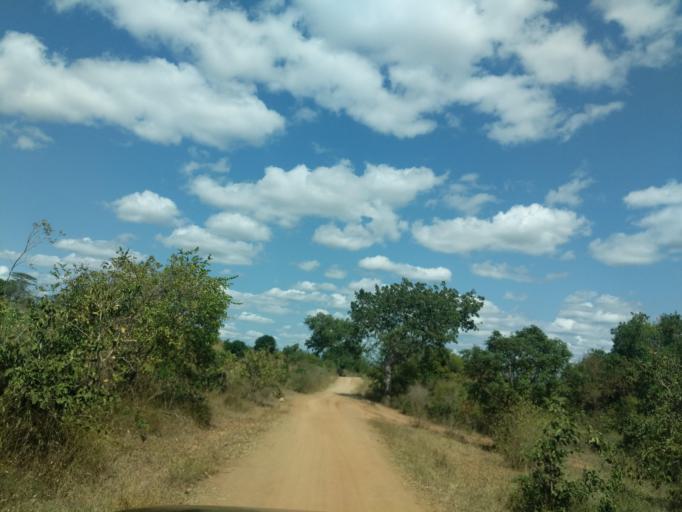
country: TZ
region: Tanga
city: Chanika
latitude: -5.5045
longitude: 38.3684
